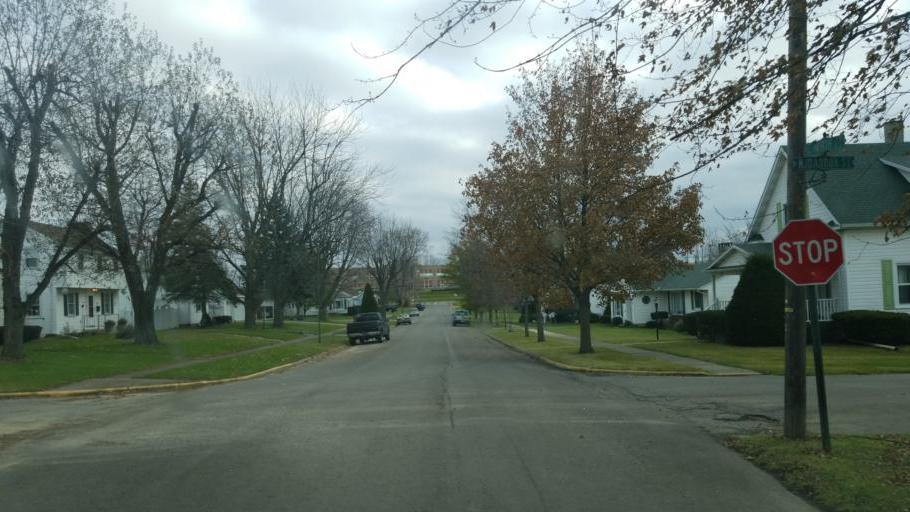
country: US
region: Ohio
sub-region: Hardin County
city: Kenton
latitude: 40.6502
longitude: -83.6023
